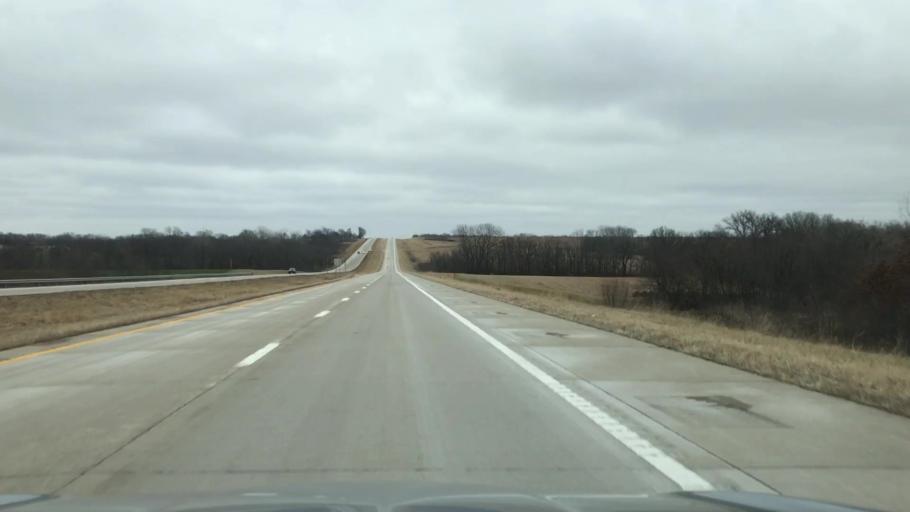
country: US
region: Missouri
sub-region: Livingston County
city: Chillicothe
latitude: 39.7377
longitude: -93.7041
